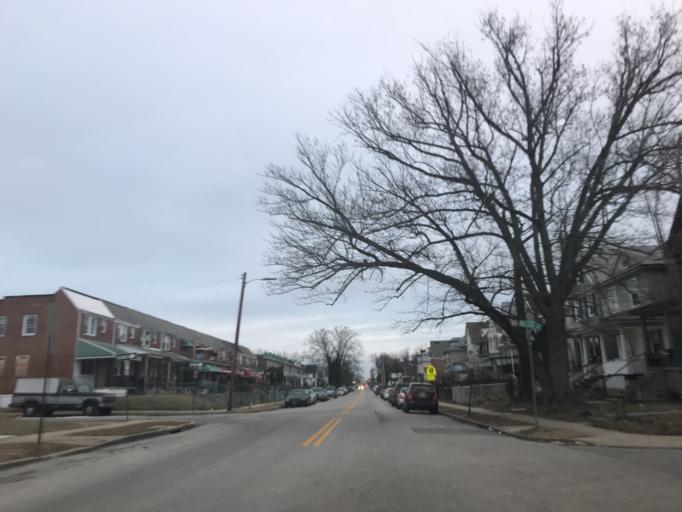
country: US
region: Maryland
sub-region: Baltimore County
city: Lochearn
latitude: 39.3465
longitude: -76.6842
